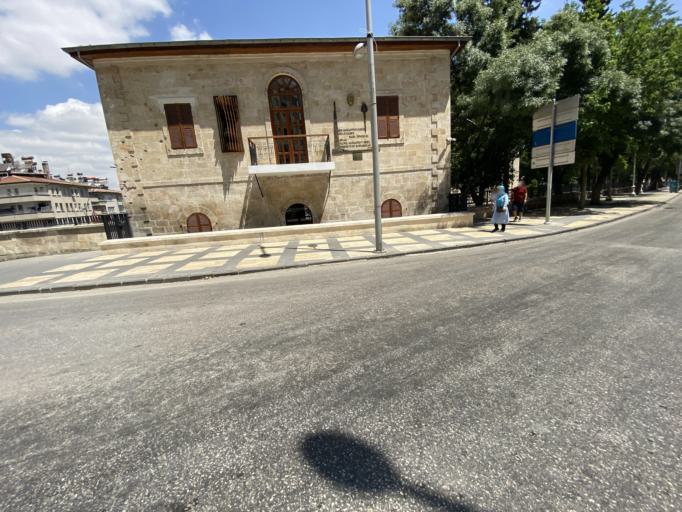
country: TR
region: Gaziantep
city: Gaziantep
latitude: 37.0623
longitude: 37.3754
